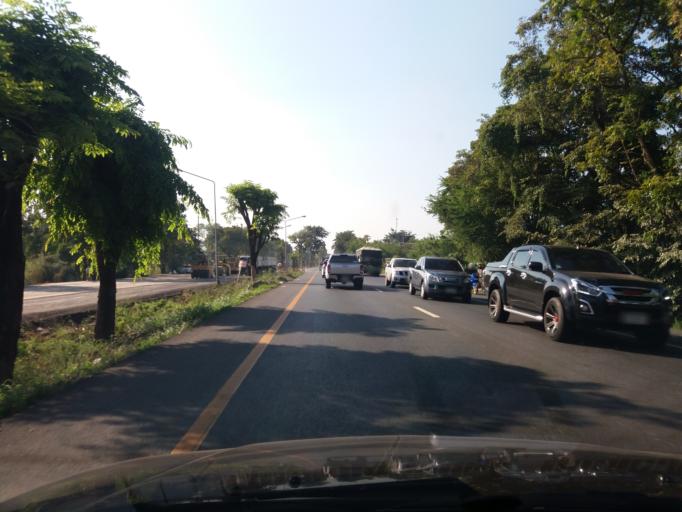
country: TH
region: Nakhon Sawan
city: Nakhon Sawan
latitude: 15.7393
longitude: 100.0175
